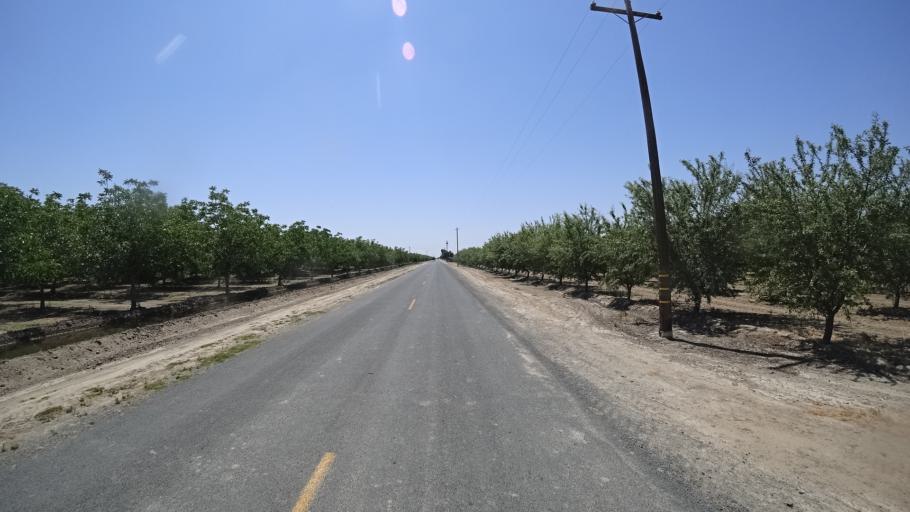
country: US
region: California
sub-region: Kings County
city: Armona
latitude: 36.2782
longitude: -119.7270
